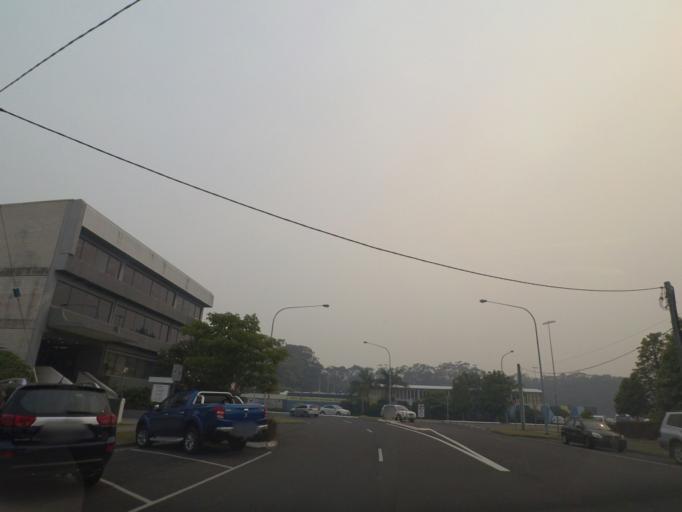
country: AU
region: New South Wales
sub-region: Coffs Harbour
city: Coffs Harbour
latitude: -30.2960
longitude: 153.1181
